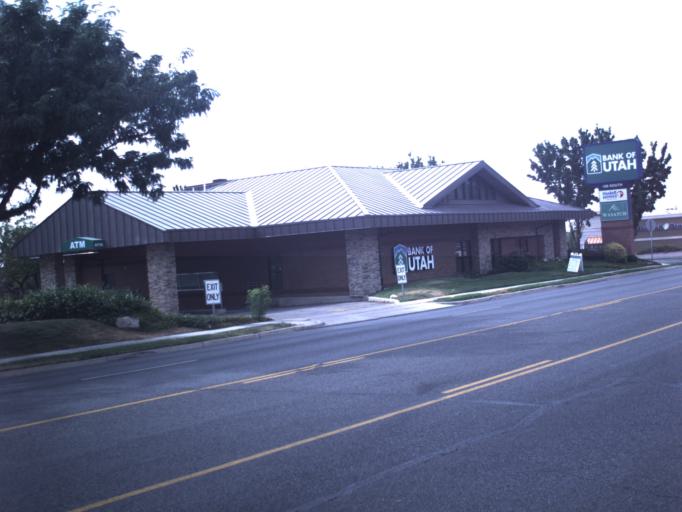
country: US
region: Utah
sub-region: Davis County
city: West Bountiful
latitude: 40.8879
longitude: -111.8921
